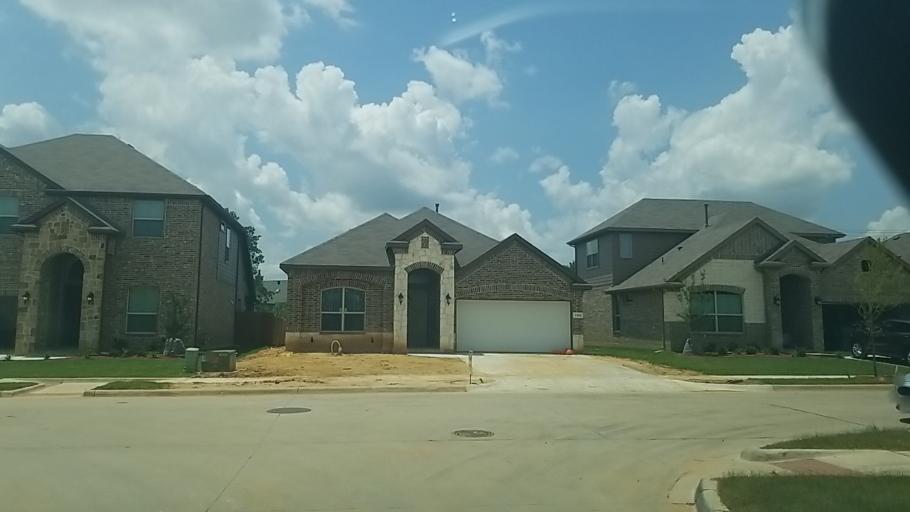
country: US
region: Texas
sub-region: Denton County
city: Denton
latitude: 33.1712
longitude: -97.1168
